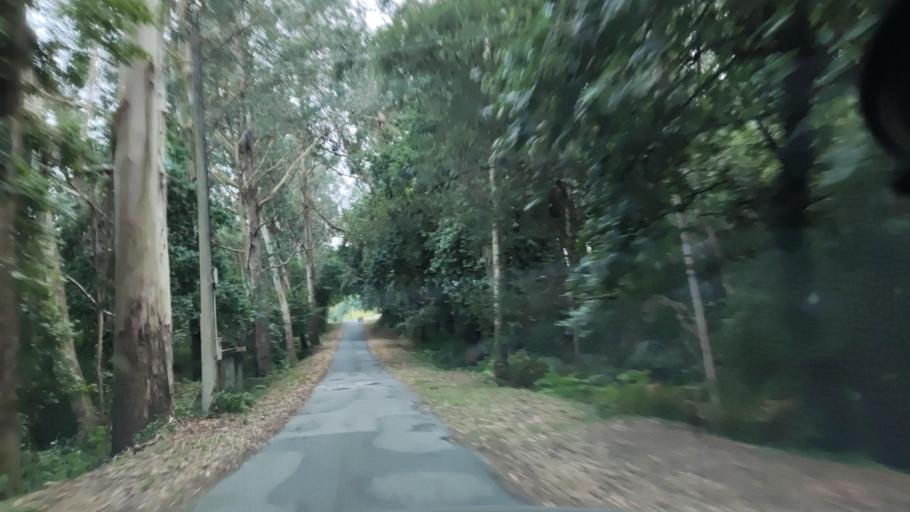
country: ES
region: Galicia
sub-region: Provincia de Pontevedra
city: Catoira
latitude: 42.7023
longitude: -8.7256
